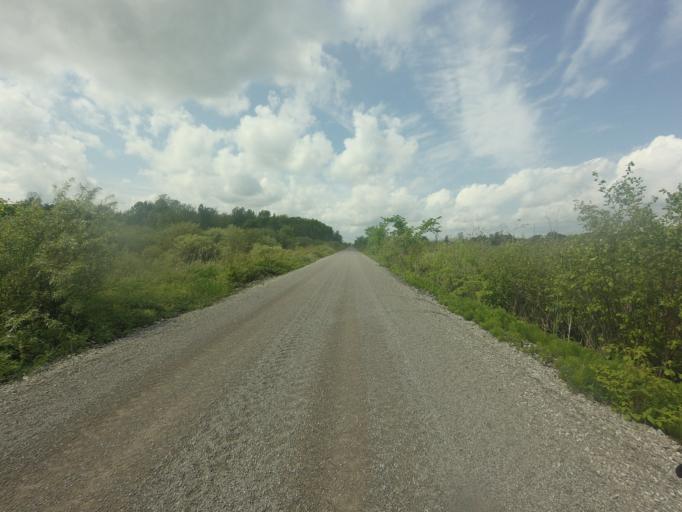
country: CA
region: Ontario
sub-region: Lanark County
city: Smiths Falls
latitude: 44.9979
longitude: -76.0657
